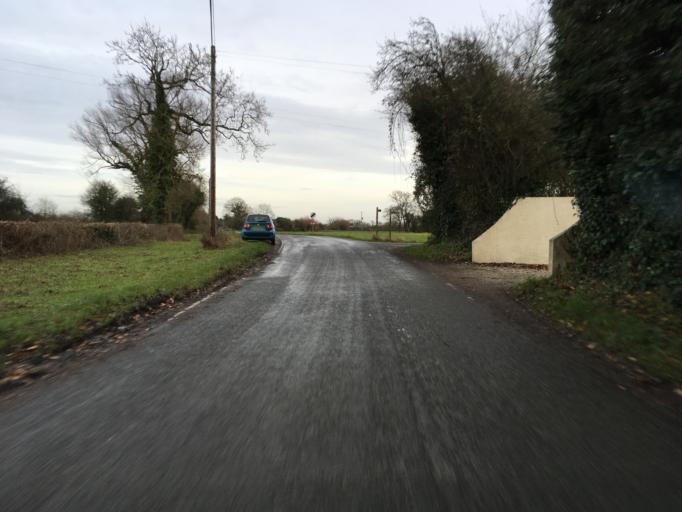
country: GB
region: Wales
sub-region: Newport
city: Goldcliff
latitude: 51.5422
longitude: -2.9105
